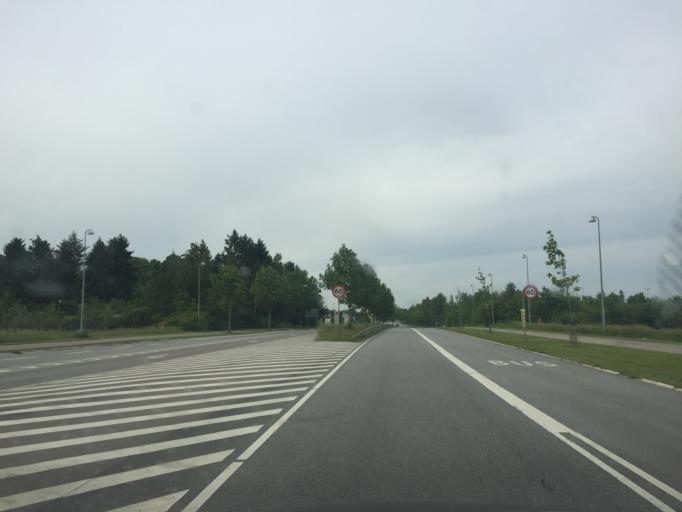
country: DK
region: Capital Region
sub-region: Hoje-Taastrup Kommune
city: Taastrup
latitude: 55.6344
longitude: 12.2877
